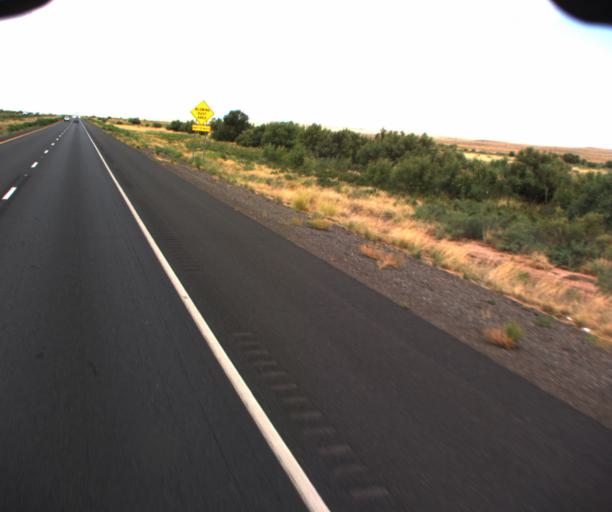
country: US
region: Arizona
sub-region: Navajo County
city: Winslow
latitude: 34.9876
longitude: -110.5613
